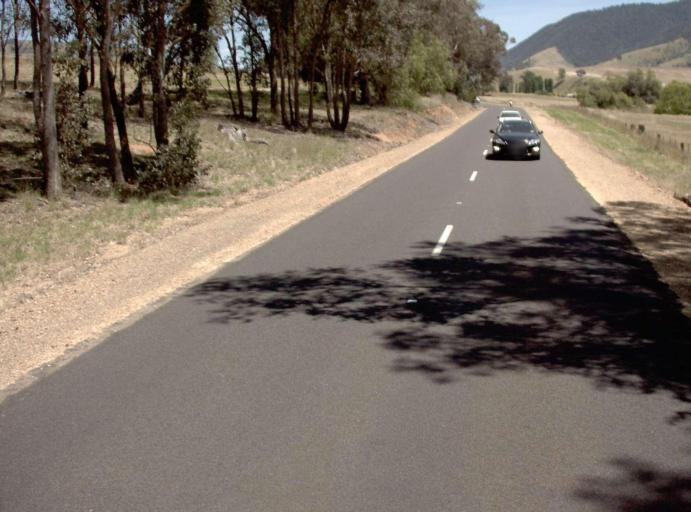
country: AU
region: Victoria
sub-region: East Gippsland
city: Bairnsdale
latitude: -37.1867
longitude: 147.7189
